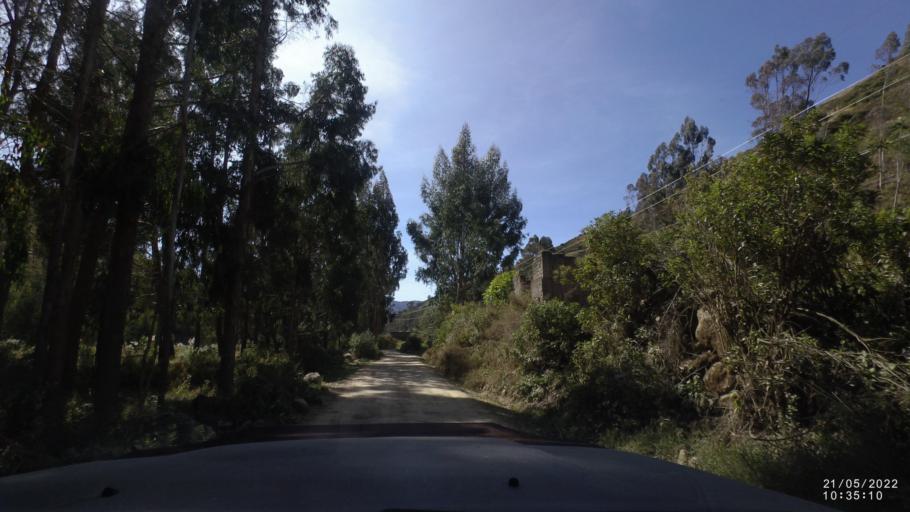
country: BO
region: Cochabamba
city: Colomi
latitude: -17.3185
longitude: -65.9288
